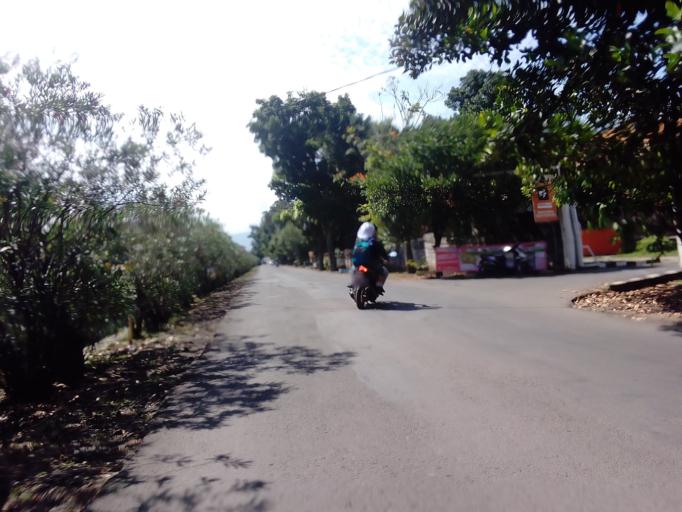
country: ID
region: West Java
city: Bandung
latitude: -6.9414
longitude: 107.6697
